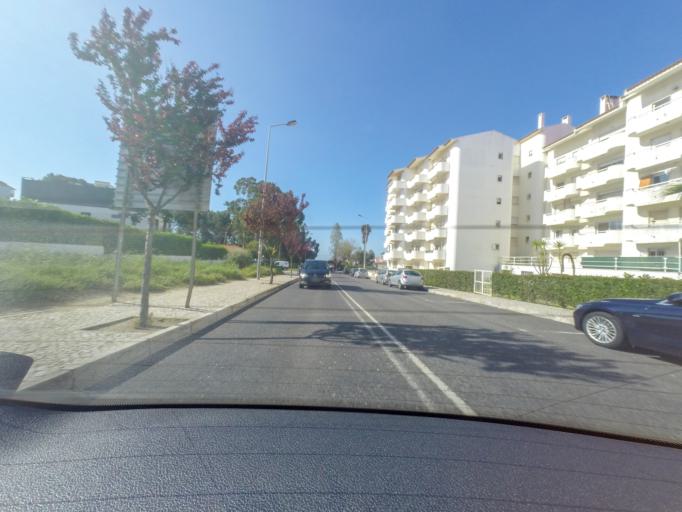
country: PT
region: Lisbon
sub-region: Cascais
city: Monte Estoril
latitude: 38.7134
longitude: -9.4177
